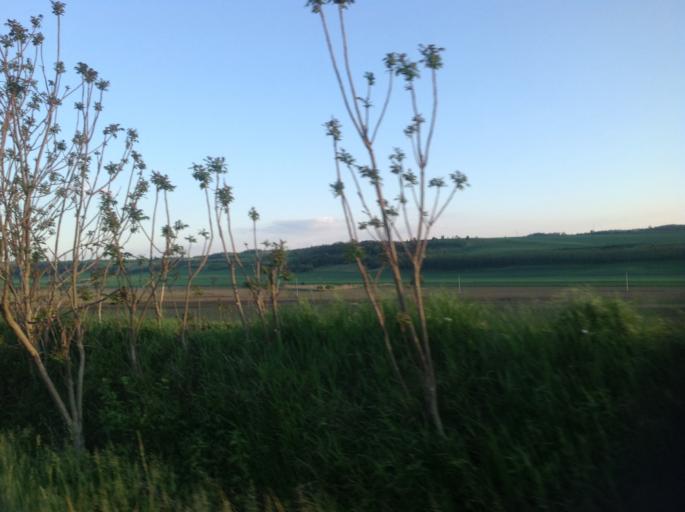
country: HU
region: Komarom-Esztergom
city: Sarisap
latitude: 47.6637
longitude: 18.6959
